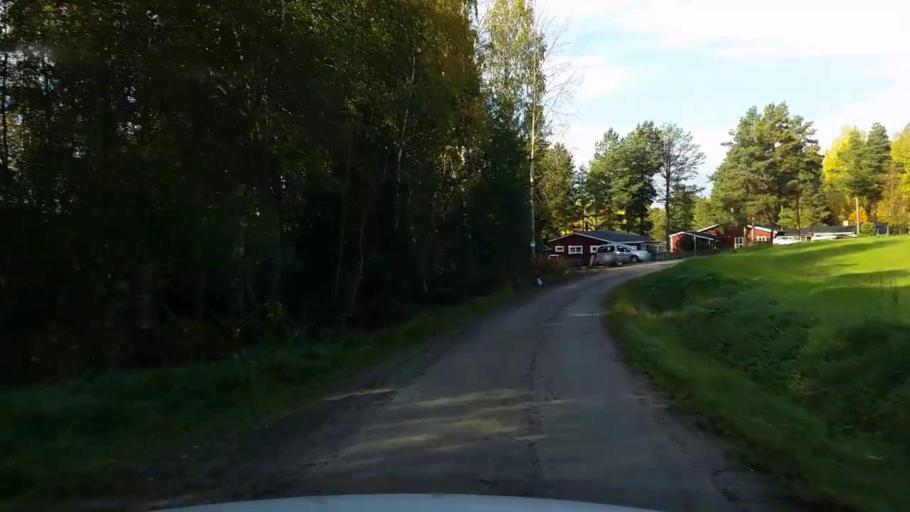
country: SE
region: Gaevleborg
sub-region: Ljusdals Kommun
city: Jaervsoe
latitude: 61.7851
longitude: 16.1546
